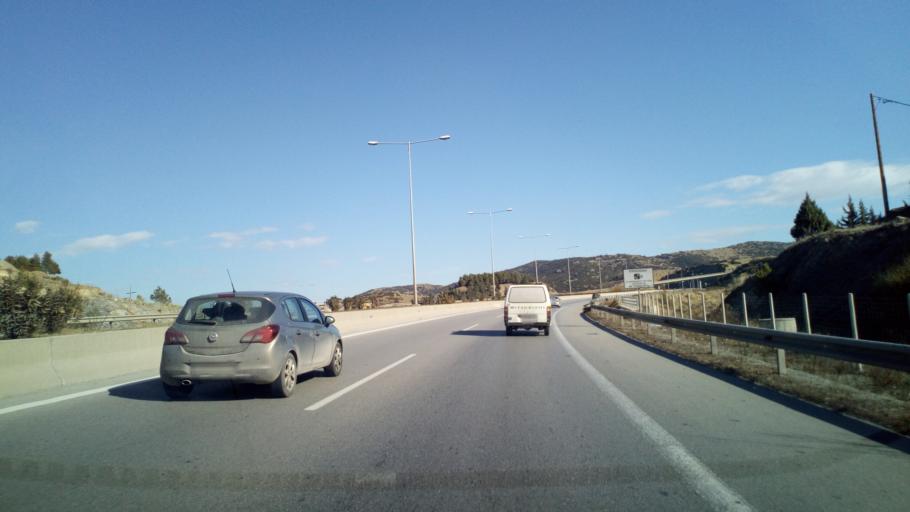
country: GR
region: Central Macedonia
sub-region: Nomos Thessalonikis
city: Efkarpia
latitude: 40.6872
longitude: 22.9592
